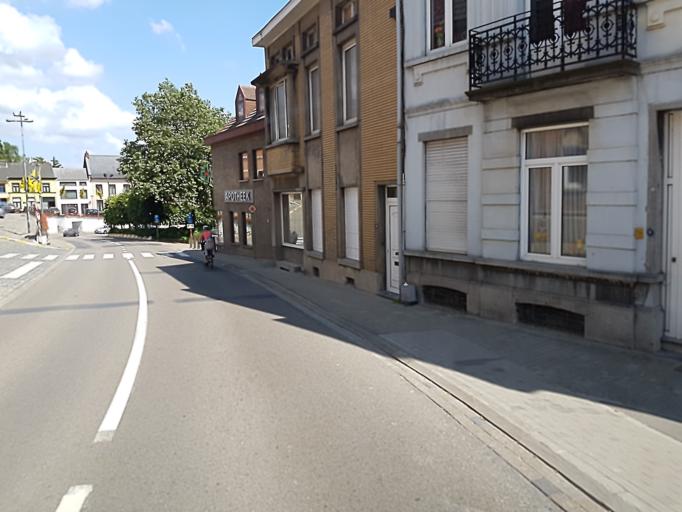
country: BE
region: Flanders
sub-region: Provincie Vlaams-Brabant
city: Overijse
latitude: 50.7731
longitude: 4.5365
